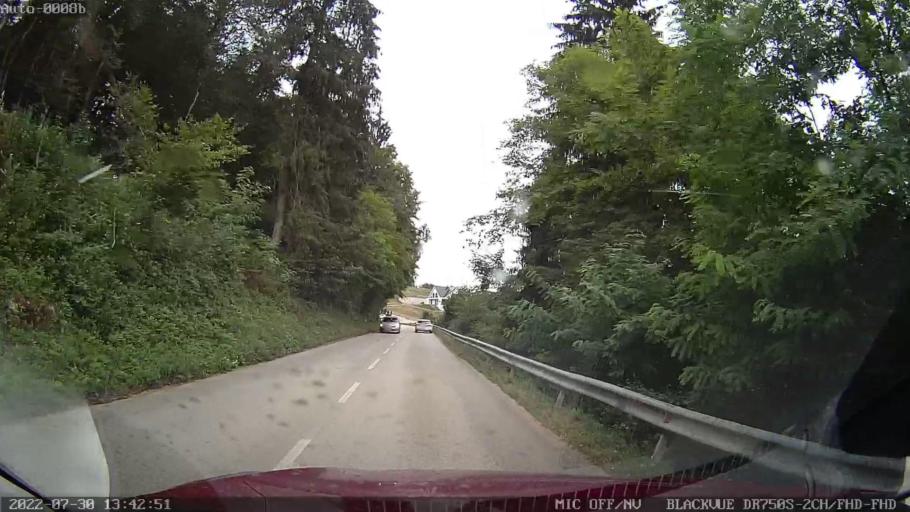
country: SI
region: Ivancna Gorica
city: Sentvid pri Sticni
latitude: 45.9090
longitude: 14.8973
